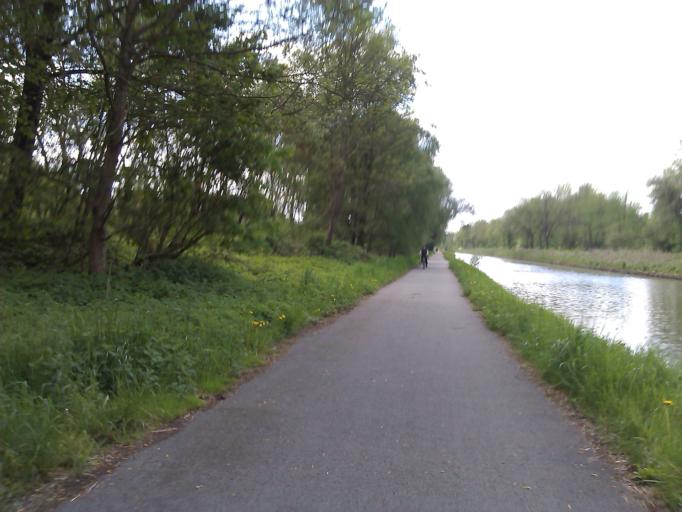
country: FR
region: Franche-Comte
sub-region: Departement du Doubs
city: Bavans
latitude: 47.4772
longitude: 6.7521
